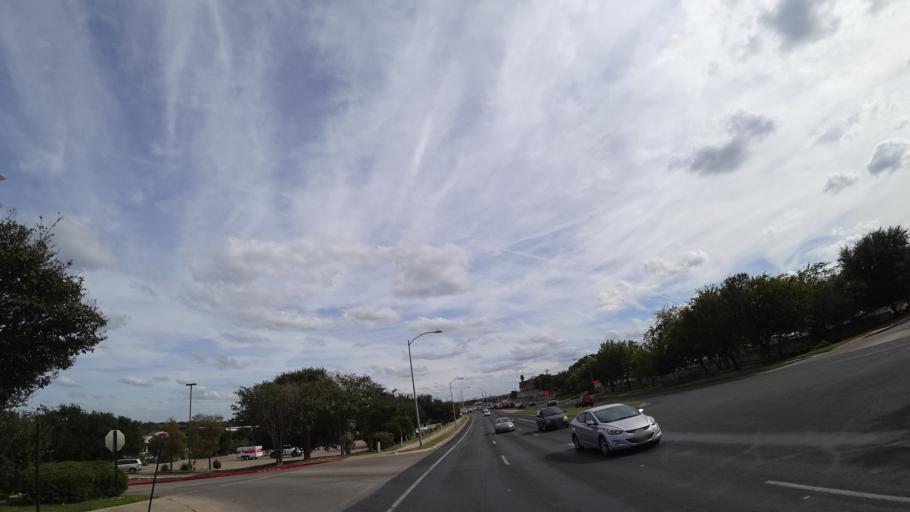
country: US
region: Texas
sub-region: Travis County
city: Onion Creek
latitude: 30.2001
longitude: -97.7661
